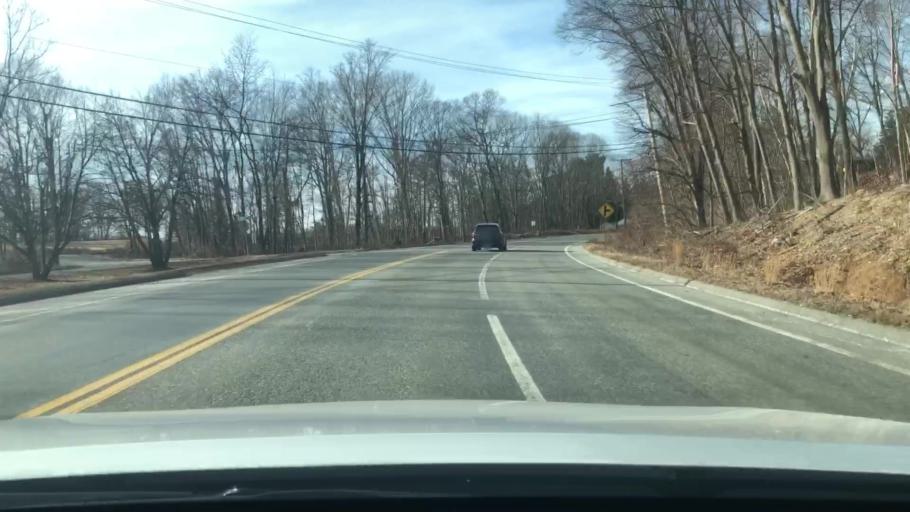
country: US
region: Massachusetts
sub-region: Worcester County
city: Grafton
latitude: 42.2047
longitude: -71.6717
